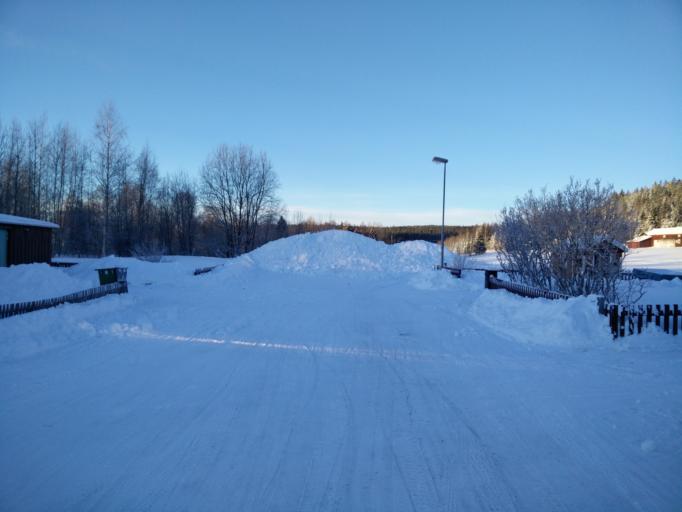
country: SE
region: Vaesternorrland
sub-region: Sundsvalls Kommun
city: Nolby
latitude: 62.2946
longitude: 17.3669
